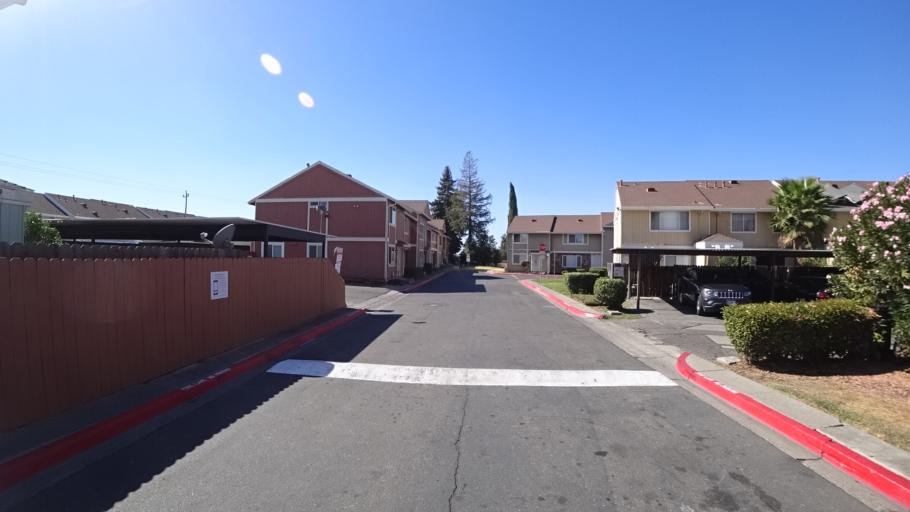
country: US
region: California
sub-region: Sacramento County
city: Parkway
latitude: 38.4825
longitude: -121.4580
